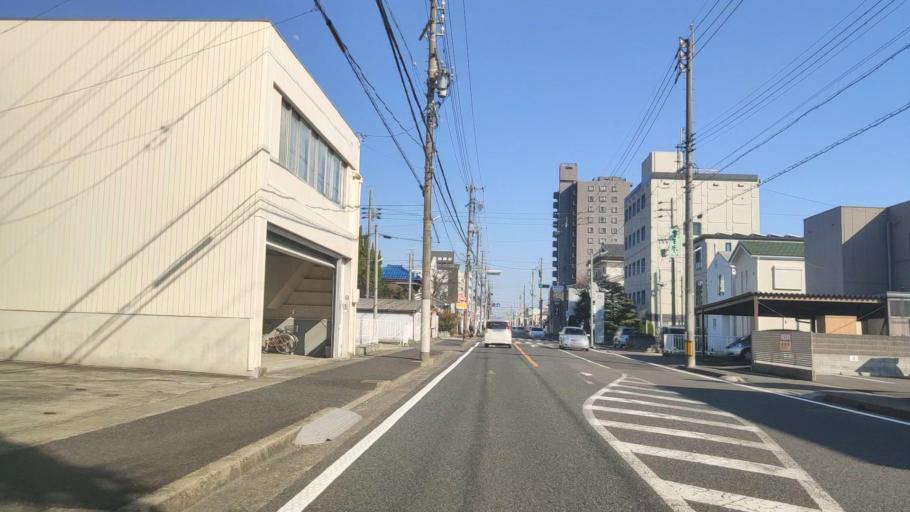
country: JP
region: Gifu
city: Gifu-shi
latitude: 35.4148
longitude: 136.7759
